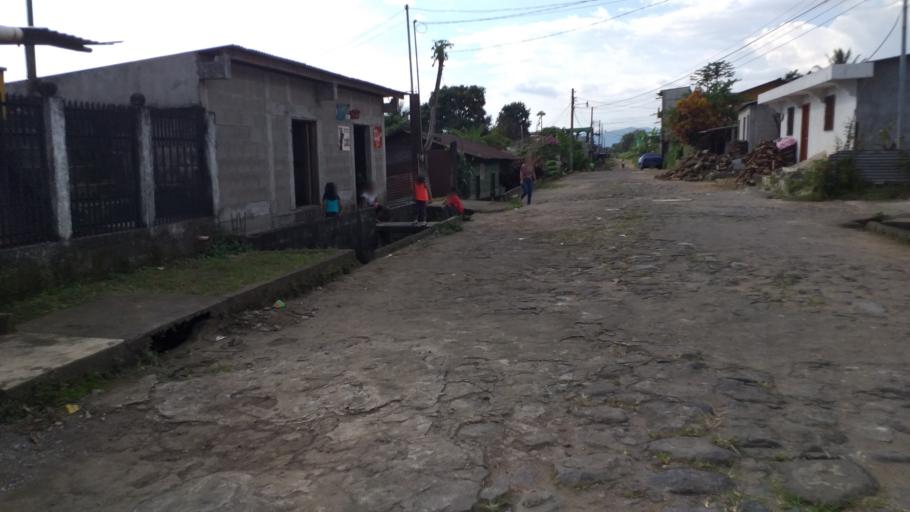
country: GT
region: Quetzaltenango
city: El Palmar
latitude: 14.6434
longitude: -91.5589
